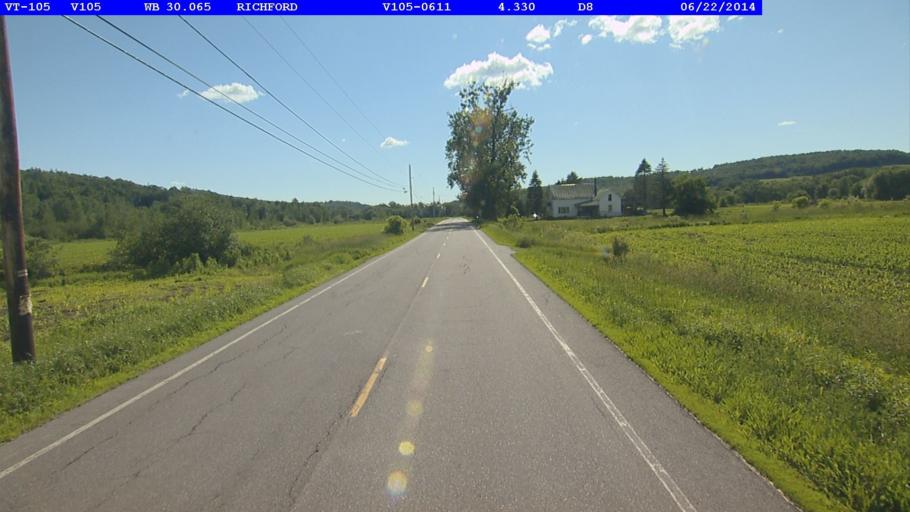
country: US
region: Vermont
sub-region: Franklin County
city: Richford
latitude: 44.9942
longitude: -72.6343
